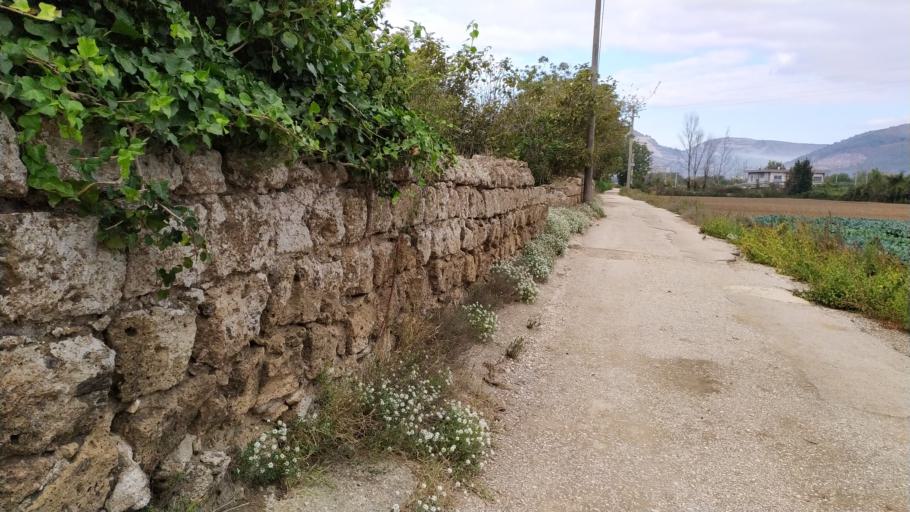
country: IT
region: Campania
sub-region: Provincia di Caserta
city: Montedecoro
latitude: 41.0162
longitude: 14.4061
